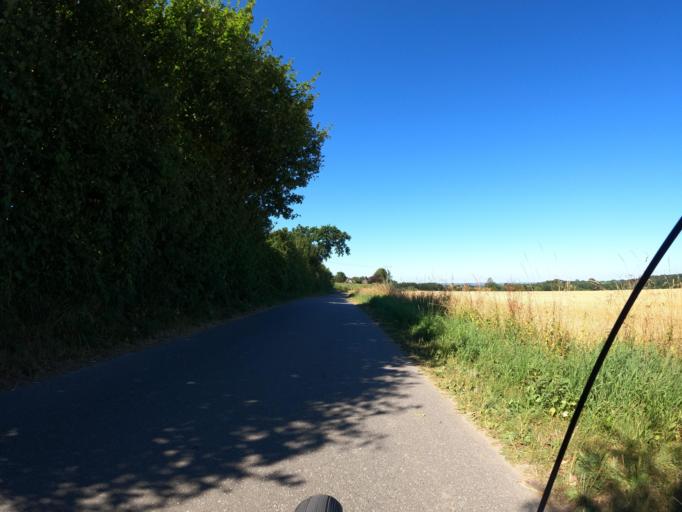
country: DE
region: Schleswig-Holstein
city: Steinbergkirche
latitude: 54.7795
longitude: 9.7605
